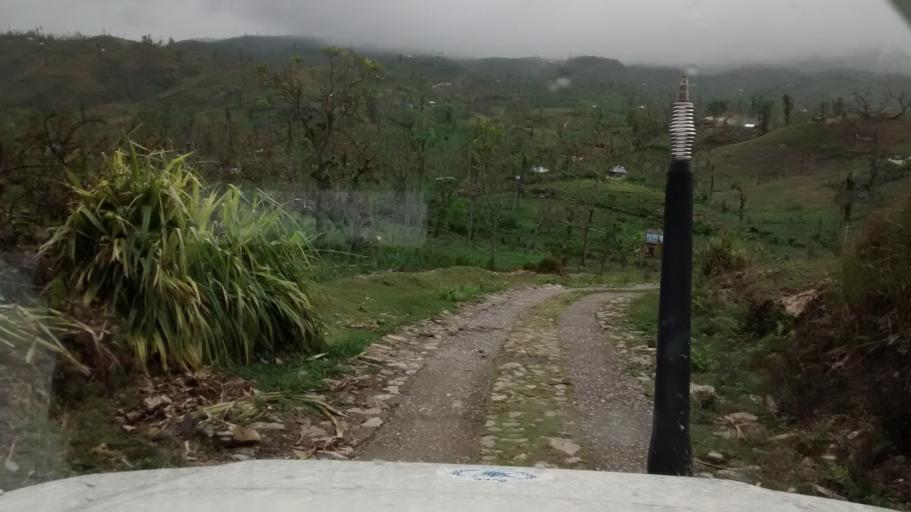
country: HT
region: Grandans
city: Moron
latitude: 18.5427
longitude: -74.1556
